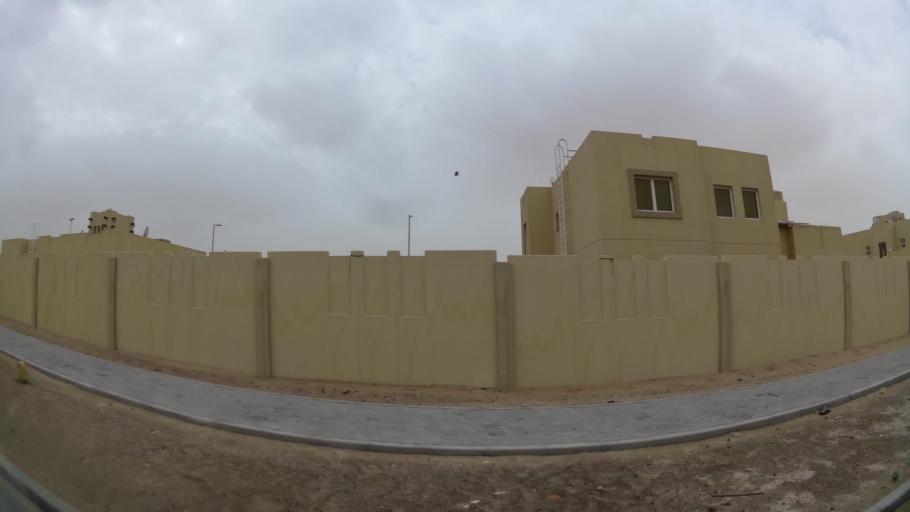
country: AE
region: Abu Dhabi
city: Abu Dhabi
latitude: 24.4425
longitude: 54.7205
